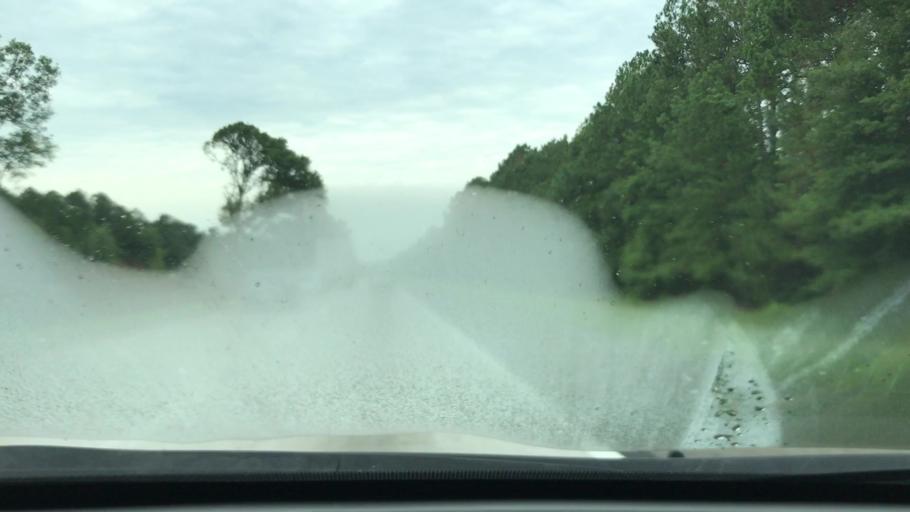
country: US
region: South Carolina
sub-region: Jasper County
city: Hardeeville
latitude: 32.3334
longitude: -81.0517
